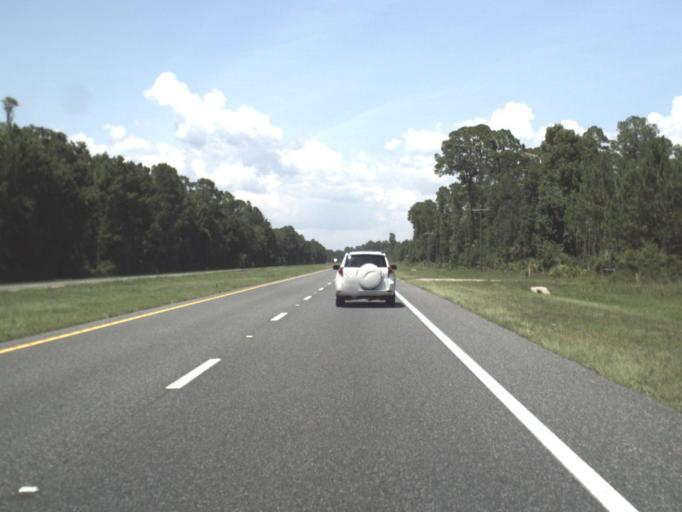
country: US
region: Florida
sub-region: Levy County
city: Inglis
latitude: 29.0800
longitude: -82.6410
